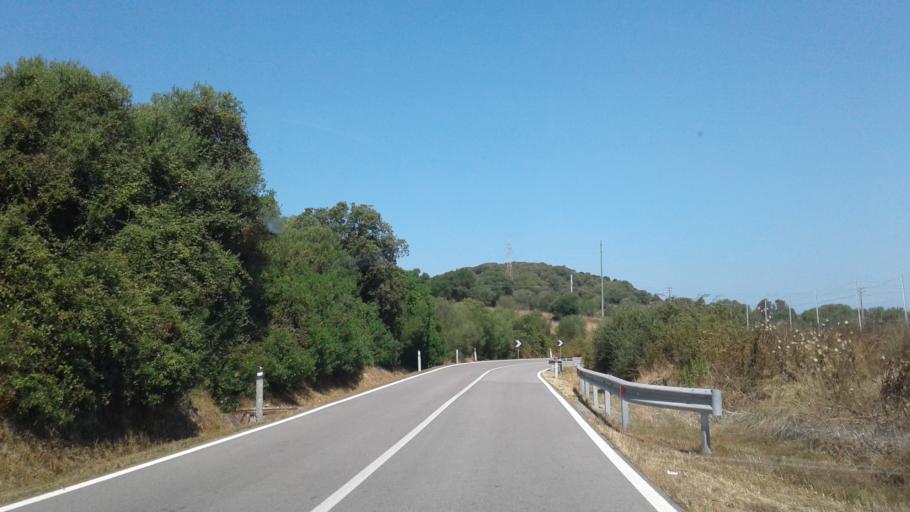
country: IT
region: Sardinia
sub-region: Provincia di Olbia-Tempio
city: Palau
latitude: 41.1586
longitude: 9.3149
